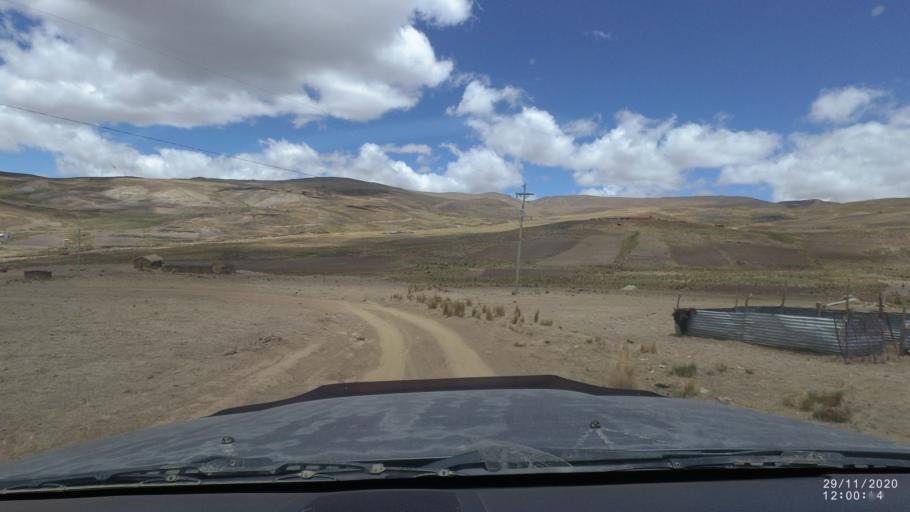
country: BO
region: Cochabamba
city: Cochabamba
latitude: -17.1532
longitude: -66.2789
